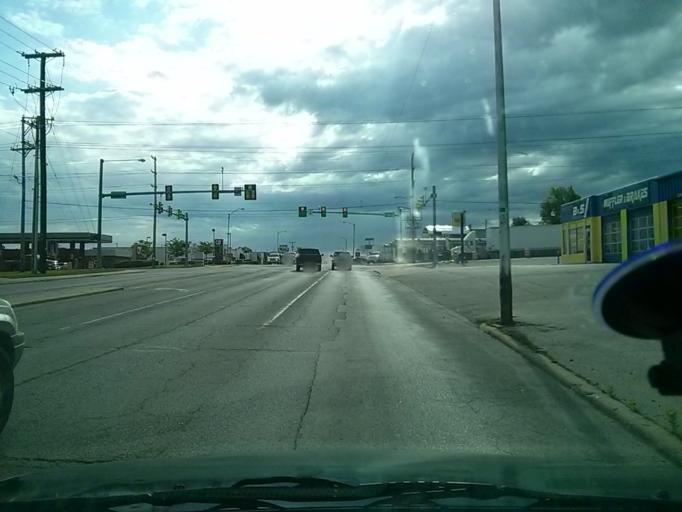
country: US
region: Oklahoma
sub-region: Tulsa County
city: Tulsa
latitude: 36.1607
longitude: -95.9233
